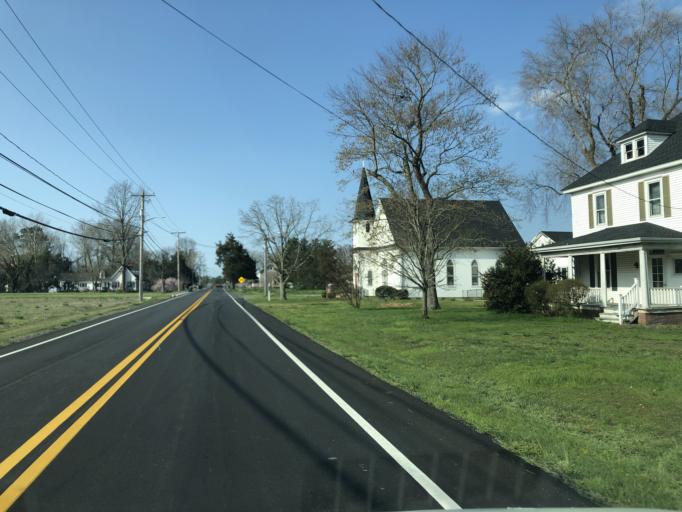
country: US
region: Maryland
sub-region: Dorchester County
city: Algonquin
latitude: 38.5052
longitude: -76.1497
